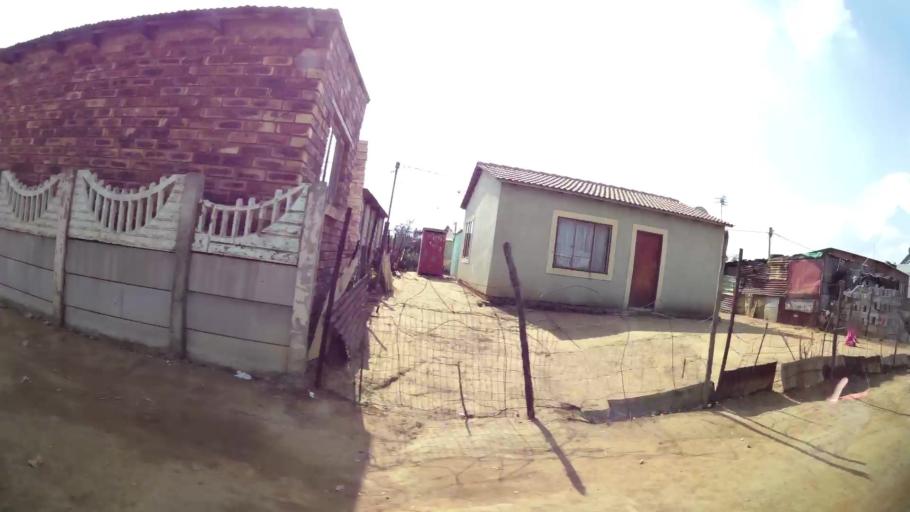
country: ZA
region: Gauteng
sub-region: Ekurhuleni Metropolitan Municipality
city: Springs
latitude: -26.1205
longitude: 28.4804
